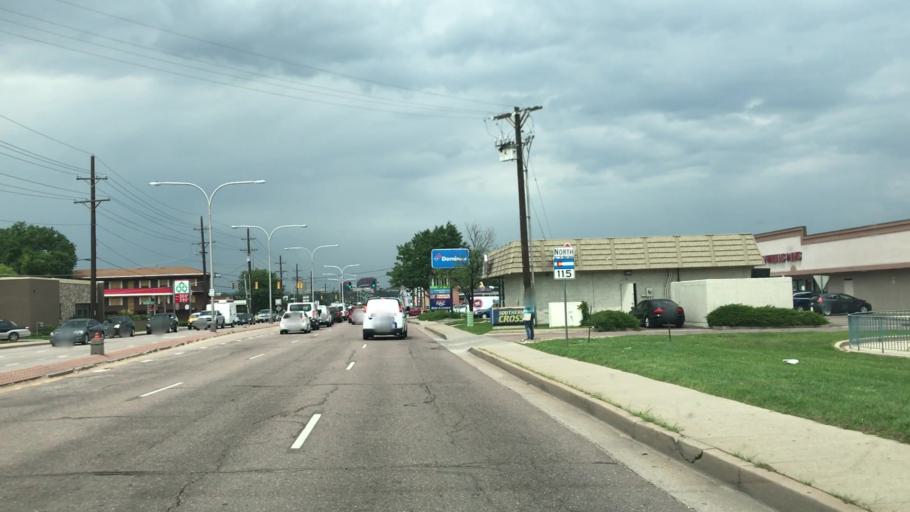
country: US
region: Colorado
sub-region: El Paso County
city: Colorado Springs
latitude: 38.8073
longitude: -104.8222
